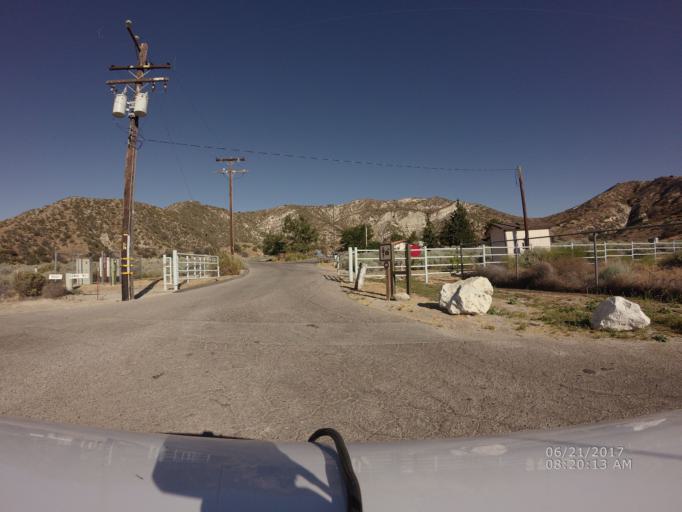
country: US
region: California
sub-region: Kern County
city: Lebec
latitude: 34.7295
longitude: -118.8020
